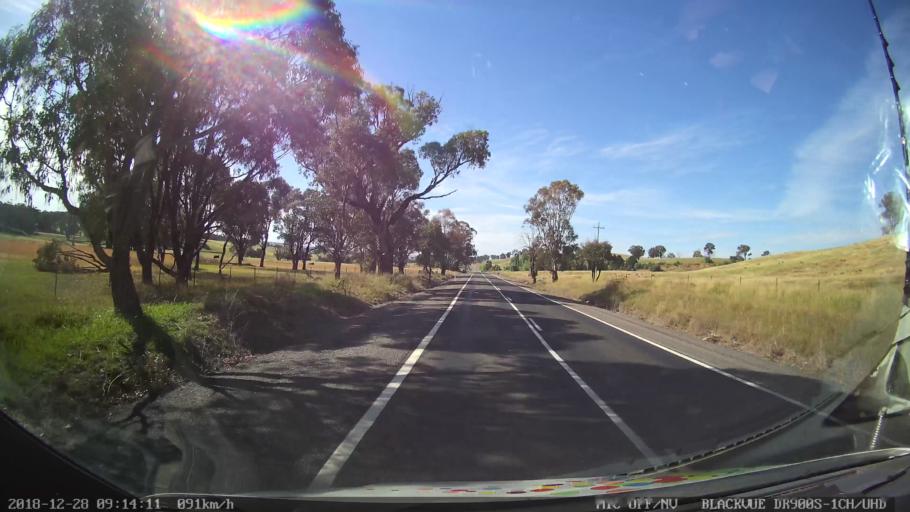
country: AU
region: New South Wales
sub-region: Upper Lachlan Shire
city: Crookwell
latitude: -34.2788
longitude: 149.3453
